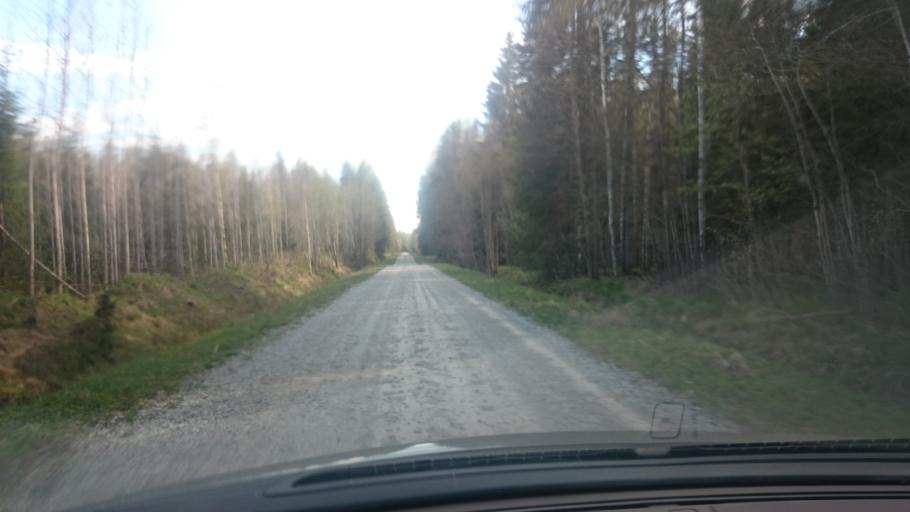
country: EE
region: Ida-Virumaa
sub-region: Sillamaee linn
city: Sillamae
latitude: 59.1560
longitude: 27.8016
